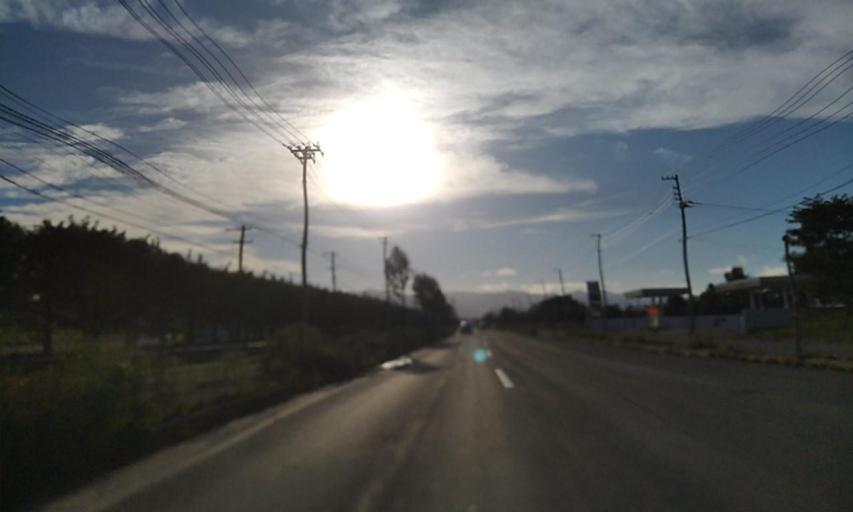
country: JP
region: Hokkaido
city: Obihiro
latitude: 42.9230
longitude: 143.0754
